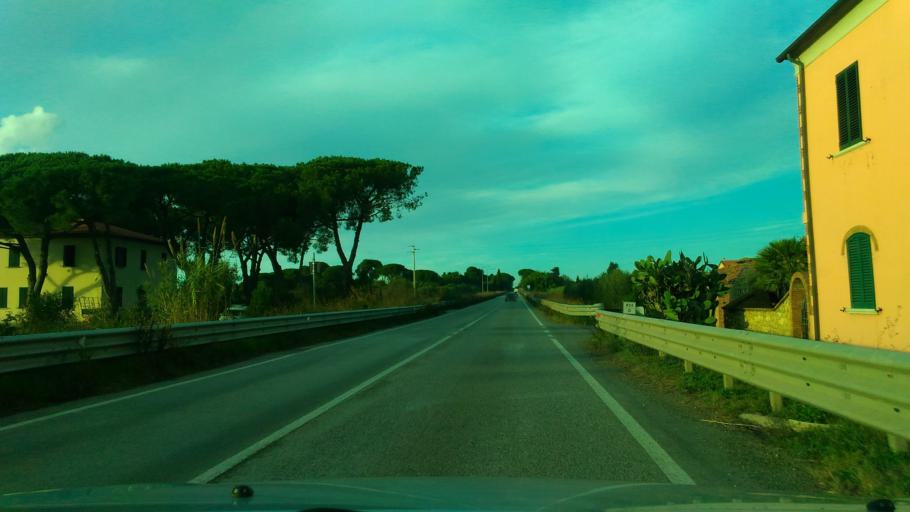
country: IT
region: Tuscany
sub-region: Provincia di Livorno
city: S.P. in Palazzi
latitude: 43.3338
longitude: 10.5061
